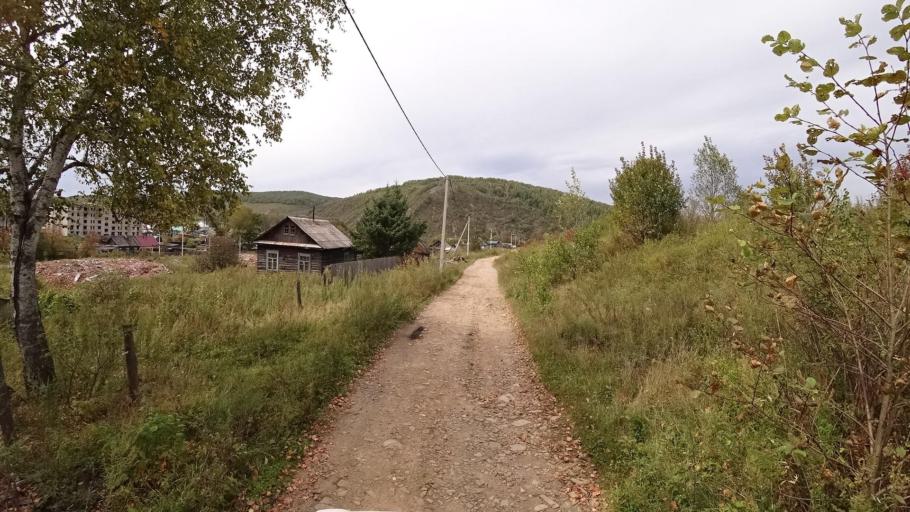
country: RU
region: Jewish Autonomous Oblast
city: Khingansk
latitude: 49.1274
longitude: 131.2019
